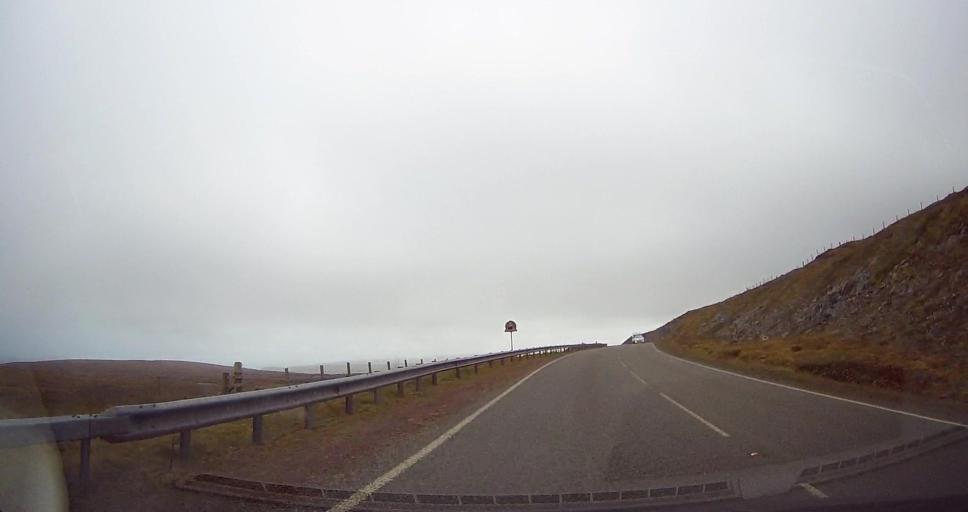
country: GB
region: Scotland
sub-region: Shetland Islands
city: Sandwick
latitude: 59.9629
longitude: -1.2826
